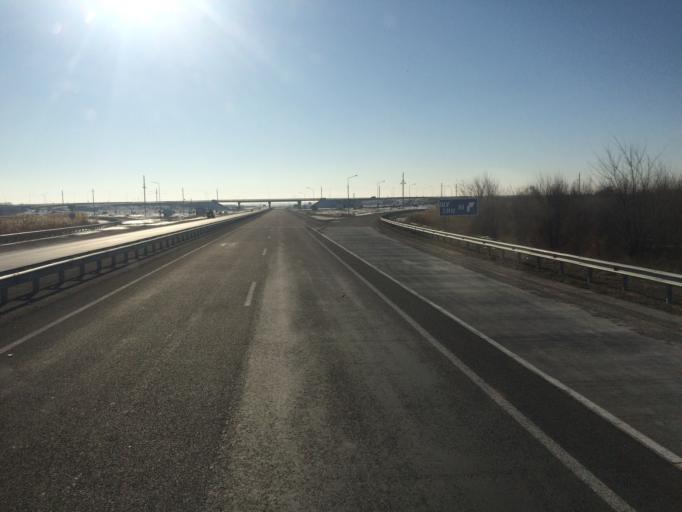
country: KG
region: Chuy
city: Sokuluk
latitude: 43.2792
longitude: 74.2337
